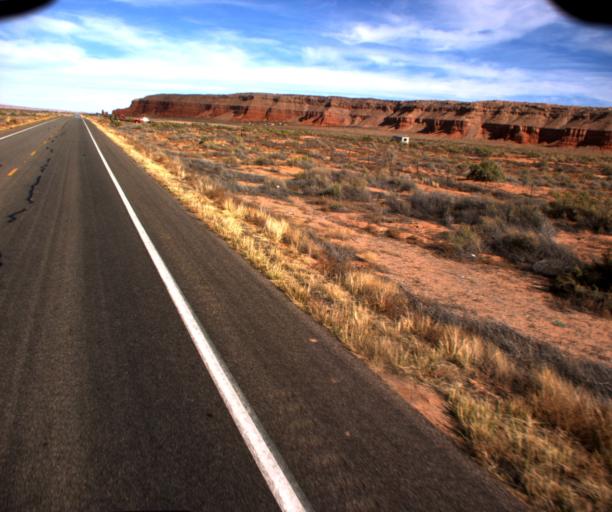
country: US
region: Arizona
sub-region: Navajo County
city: Kayenta
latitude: 36.7625
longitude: -110.0403
